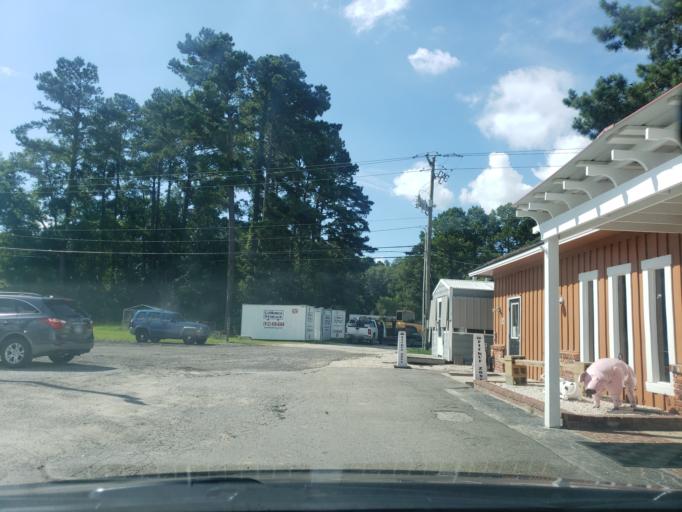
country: US
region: Georgia
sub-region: Chatham County
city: Georgetown
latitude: 31.9967
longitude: -81.2616
